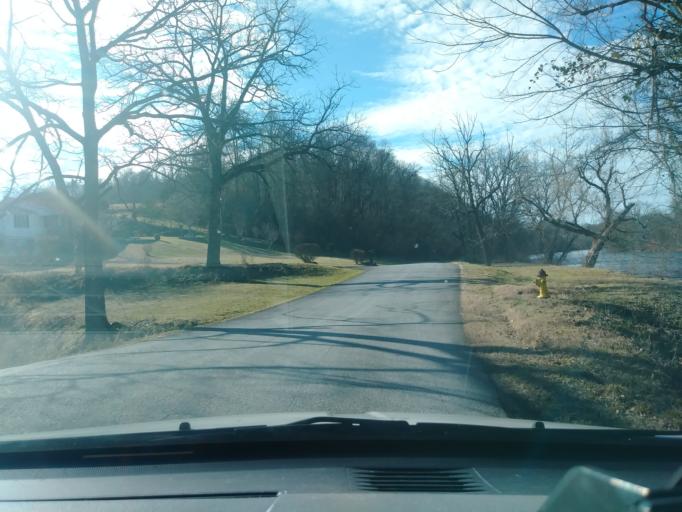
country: US
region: Tennessee
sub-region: Cocke County
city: Newport
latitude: 35.9780
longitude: -83.1490
